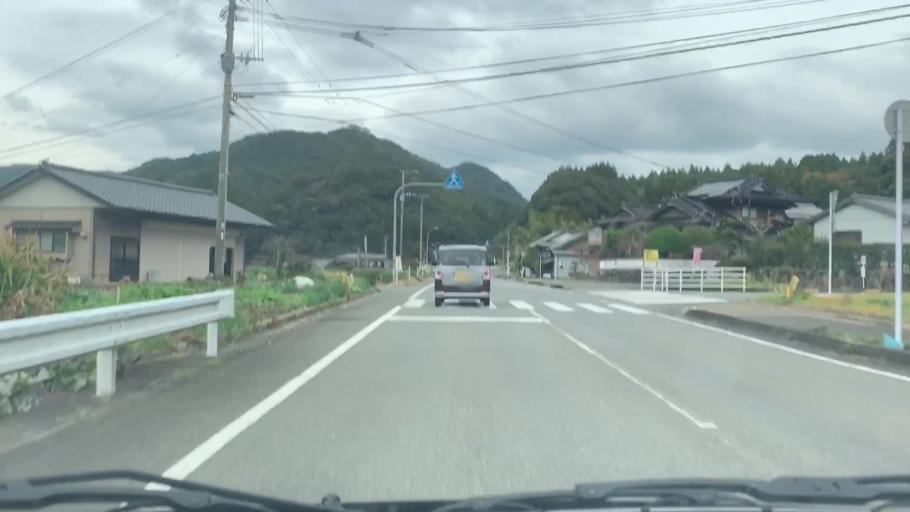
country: JP
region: Saga Prefecture
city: Ureshinomachi-shimojuku
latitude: 33.0912
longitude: 130.0267
